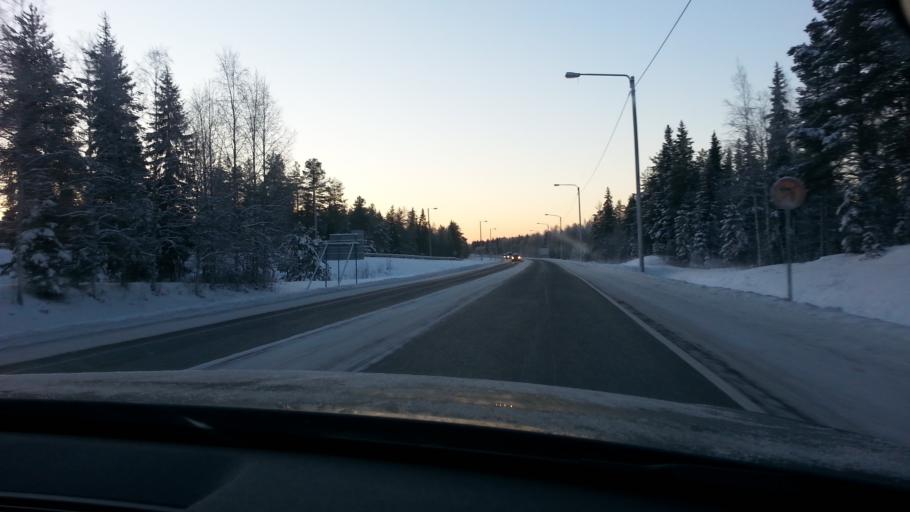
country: FI
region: Lapland
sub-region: Rovaniemi
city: Rovaniemi
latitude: 66.5312
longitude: 25.7663
